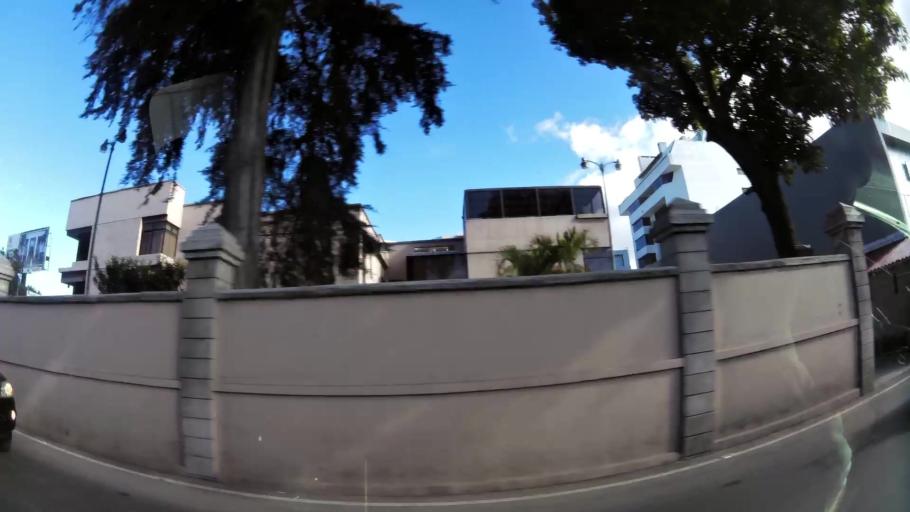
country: GT
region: Guatemala
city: Santa Catarina Pinula
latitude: 14.5898
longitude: -90.5096
